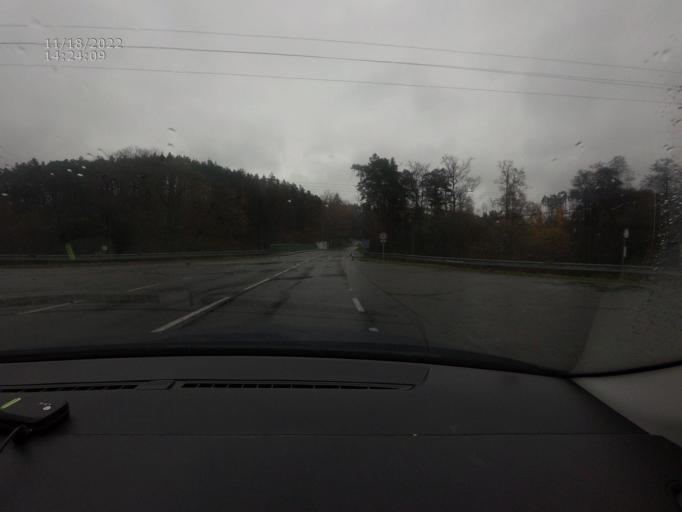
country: CZ
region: Jihocesky
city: Cimelice
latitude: 49.4386
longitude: 14.1263
